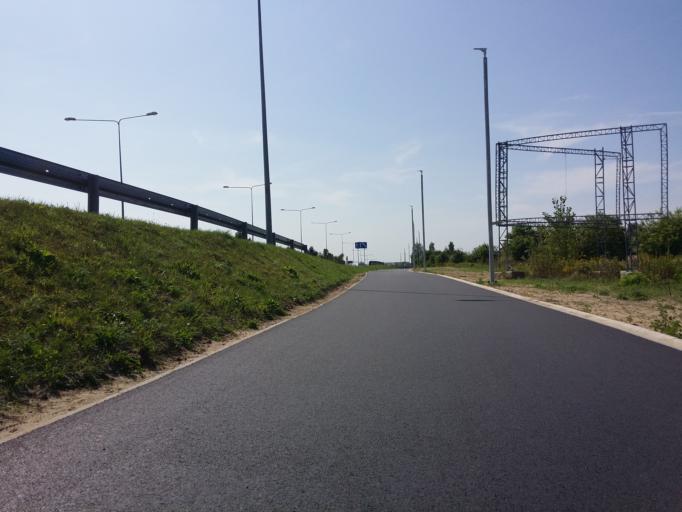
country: PL
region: Masovian Voivodeship
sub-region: Powiat radomski
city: Trablice
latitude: 51.3708
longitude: 21.1542
